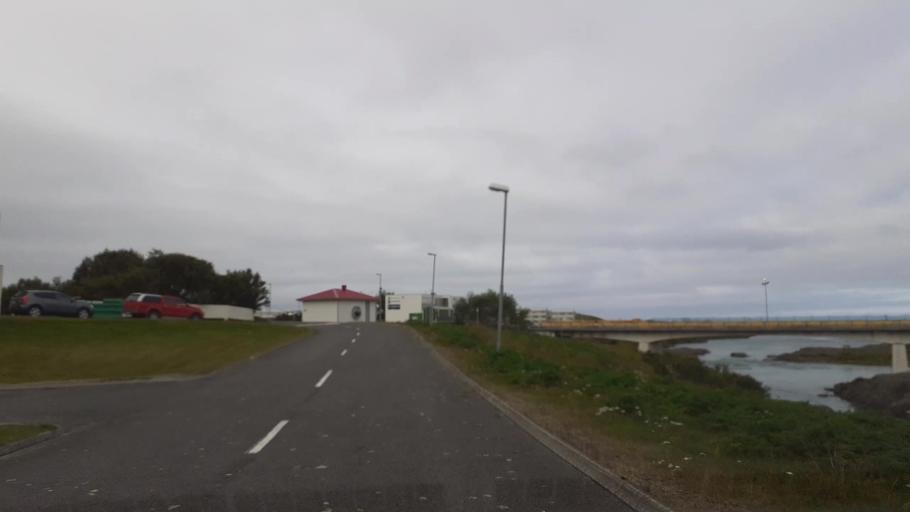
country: IS
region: Northwest
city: Saudarkrokur
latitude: 65.6570
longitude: -20.2796
